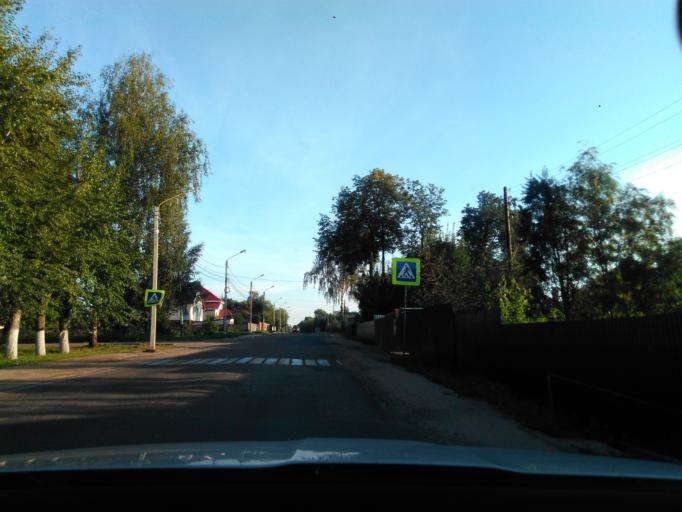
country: RU
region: Tverskaya
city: Konakovo
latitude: 56.6992
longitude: 36.7671
